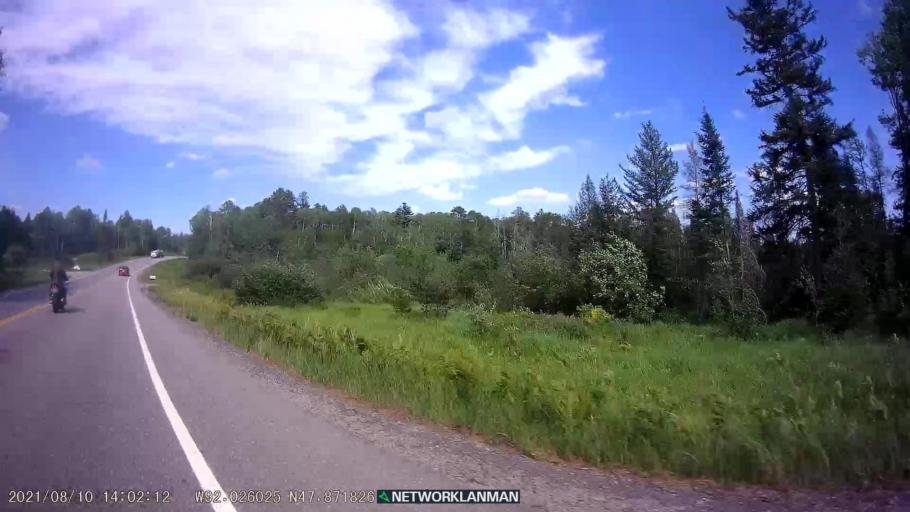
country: US
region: Minnesota
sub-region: Saint Louis County
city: Ely
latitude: 47.8719
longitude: -92.0256
